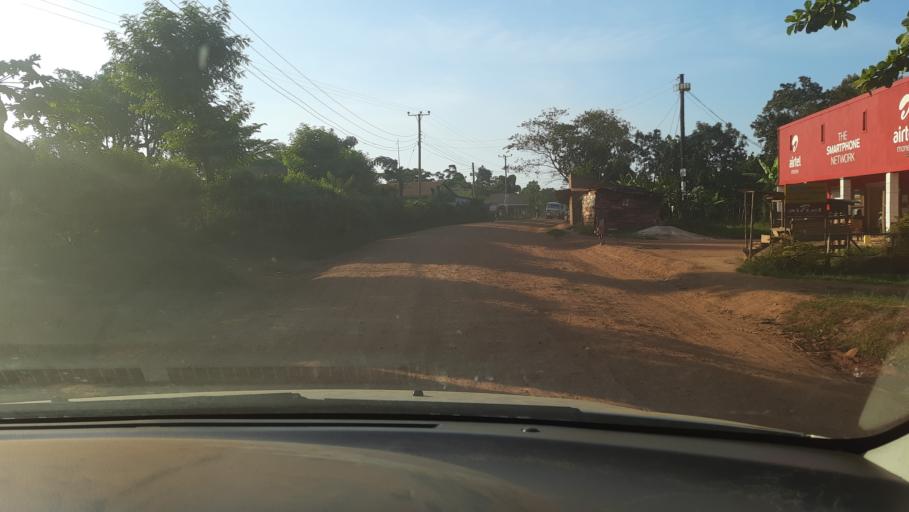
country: UG
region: Central Region
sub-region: Mukono District
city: Mukono
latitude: 0.3729
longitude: 32.7482
